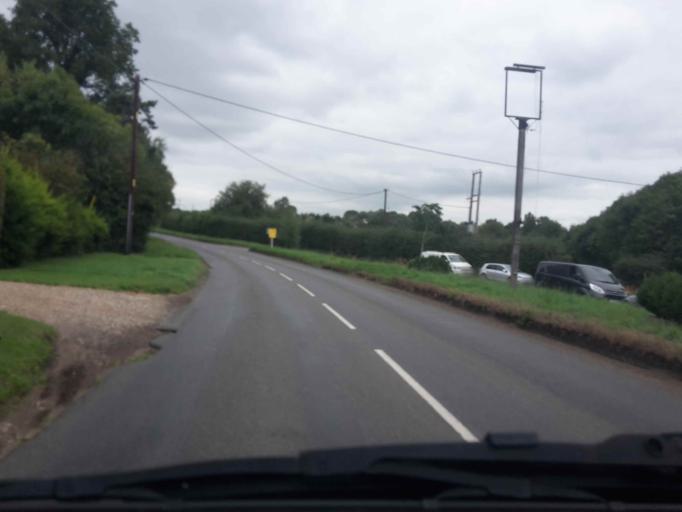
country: GB
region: England
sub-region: Oxfordshire
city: Rotherfield Peppard
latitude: 51.5320
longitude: -0.9779
